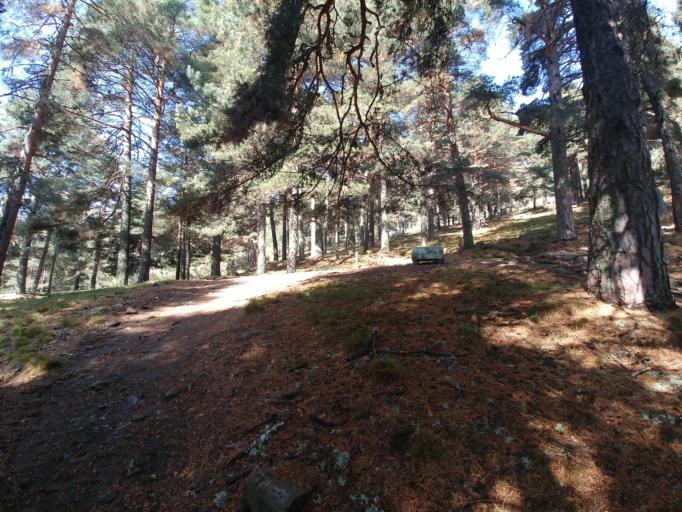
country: ES
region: Castille and Leon
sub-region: Provincia de Avila
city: Navarredonda de Gredos
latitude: 40.3528
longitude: -5.1128
